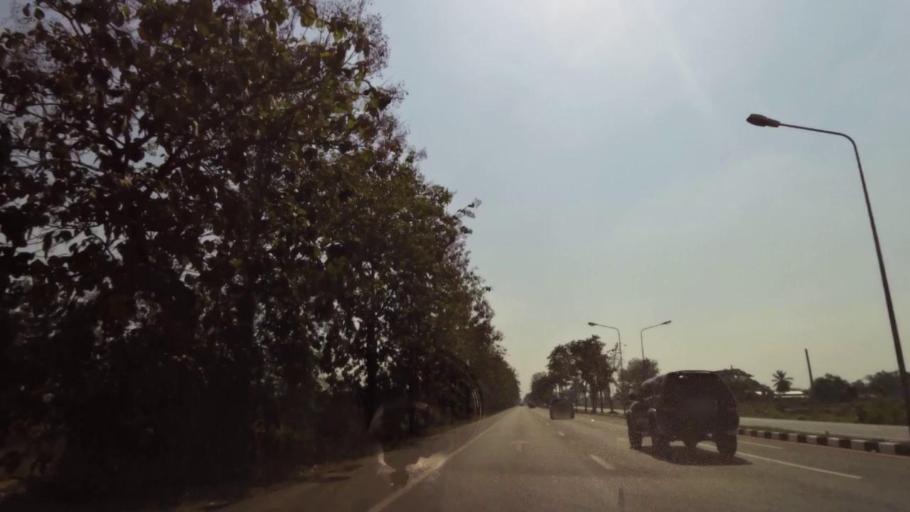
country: TH
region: Phichit
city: Bueng Na Rang
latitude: 16.0902
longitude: 100.1251
